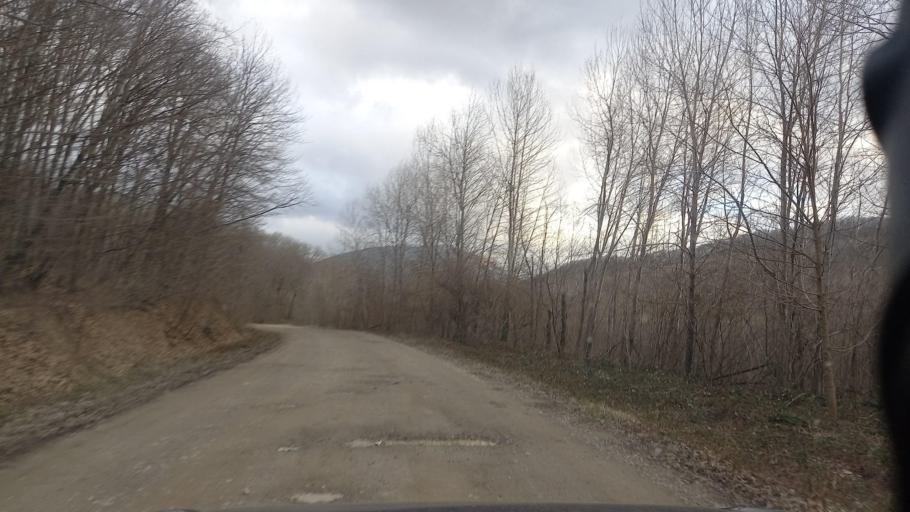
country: RU
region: Krasnodarskiy
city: Lermontovo
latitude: 44.4775
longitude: 38.8036
